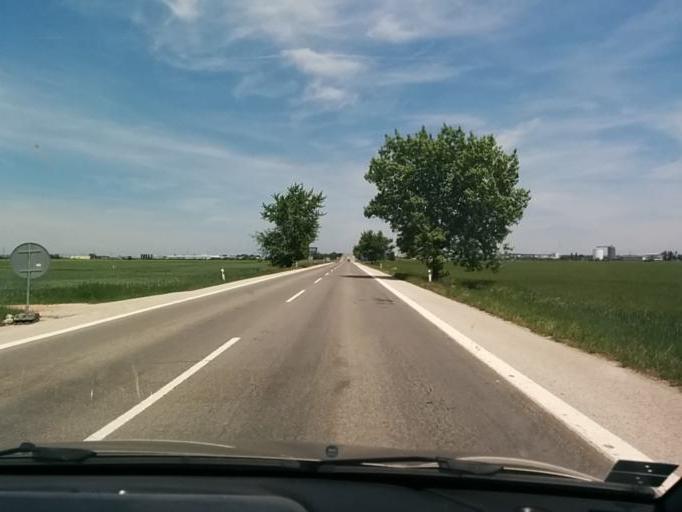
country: SK
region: Trnavsky
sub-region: Okres Galanta
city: Galanta
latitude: 48.2633
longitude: 17.7146
